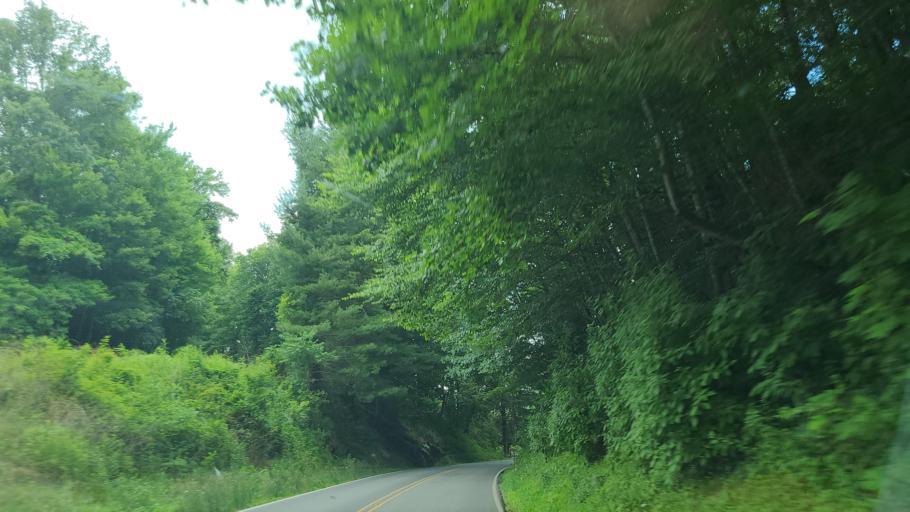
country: US
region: North Carolina
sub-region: Ashe County
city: Jefferson
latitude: 36.3938
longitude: -81.3426
